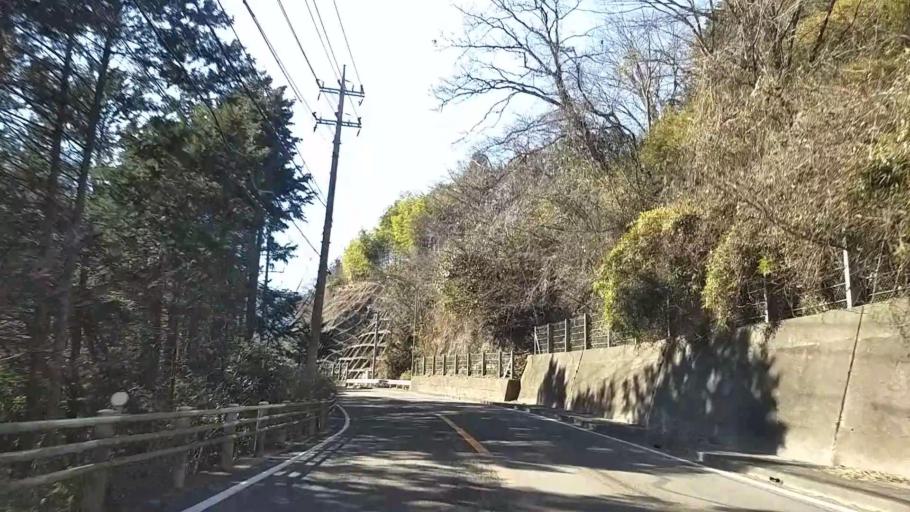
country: JP
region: Yamanashi
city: Uenohara
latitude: 35.6091
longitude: 139.0605
